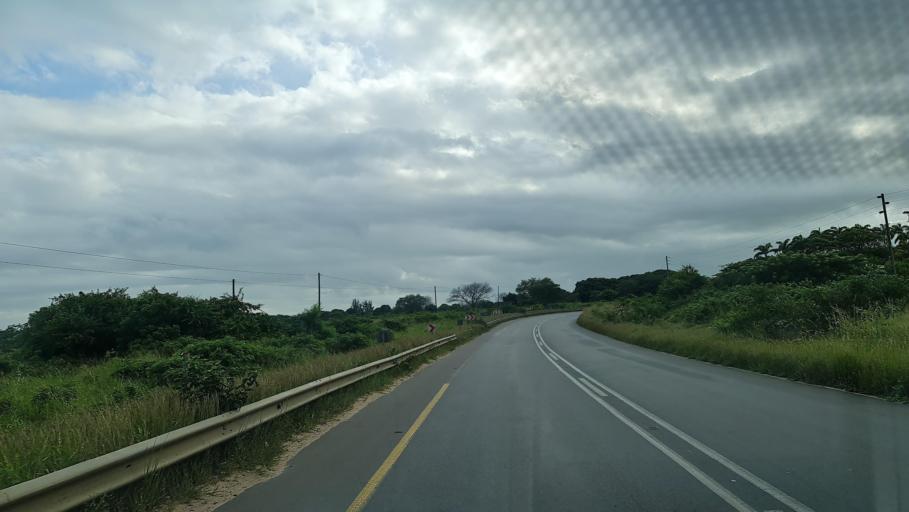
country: MZ
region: Maputo
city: Manhica
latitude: -25.4111
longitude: 32.7439
